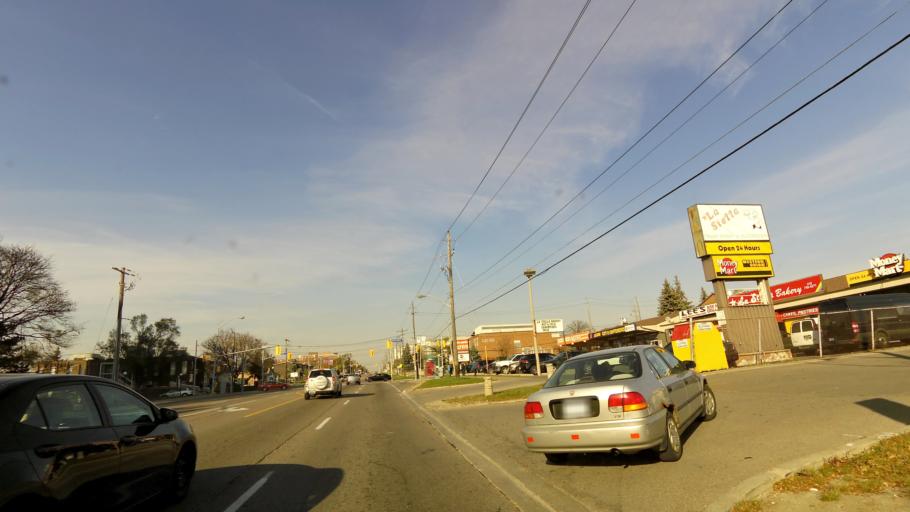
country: CA
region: Ontario
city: Concord
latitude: 43.7405
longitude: -79.5134
